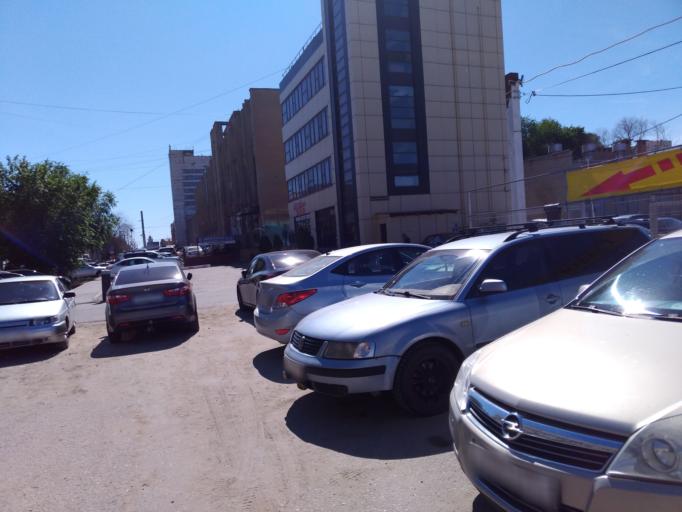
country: RU
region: Volgograd
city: Volgograd
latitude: 48.7143
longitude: 44.5198
